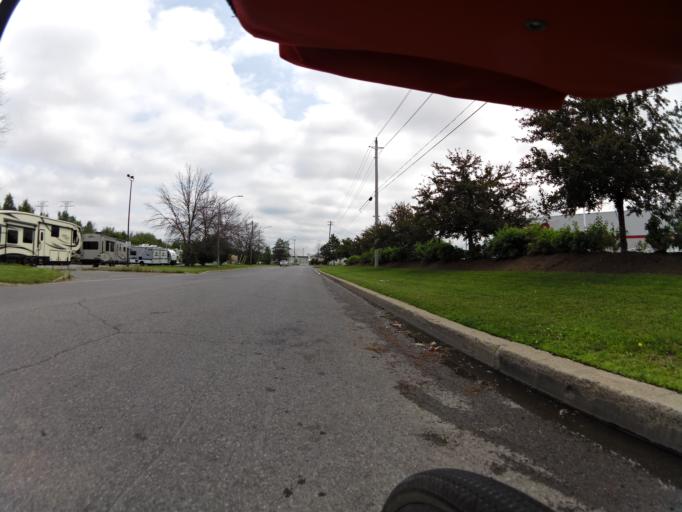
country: CA
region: Ontario
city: Ottawa
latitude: 45.3387
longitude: -75.7229
